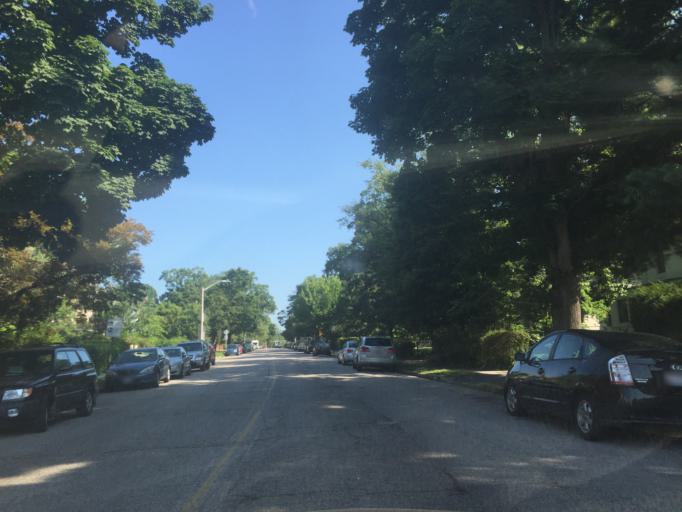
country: US
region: Maryland
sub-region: City of Baltimore
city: Baltimore
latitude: 39.3383
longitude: -76.6333
